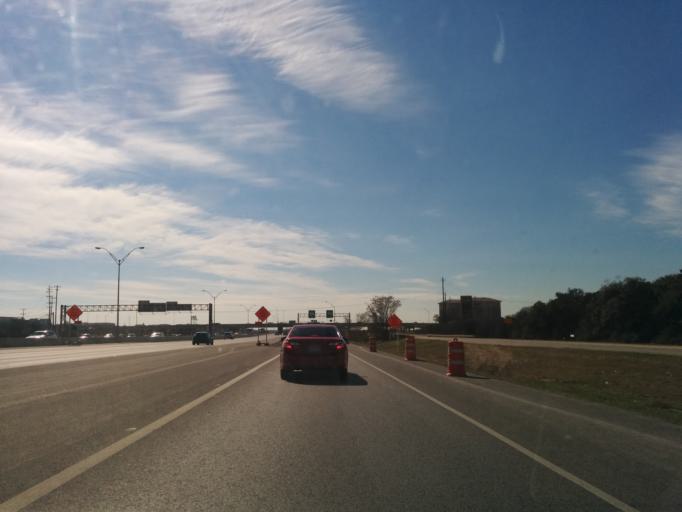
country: US
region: Texas
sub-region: Bexar County
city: Shavano Park
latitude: 29.5952
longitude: -98.5994
